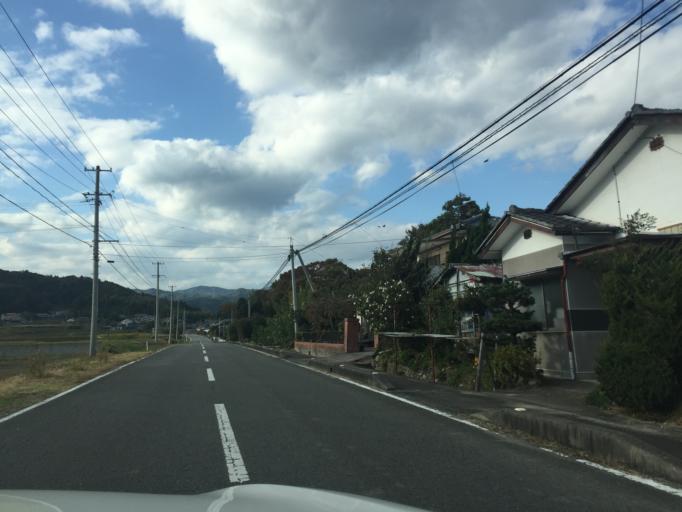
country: JP
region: Fukushima
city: Iwaki
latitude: 37.1353
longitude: 140.8477
